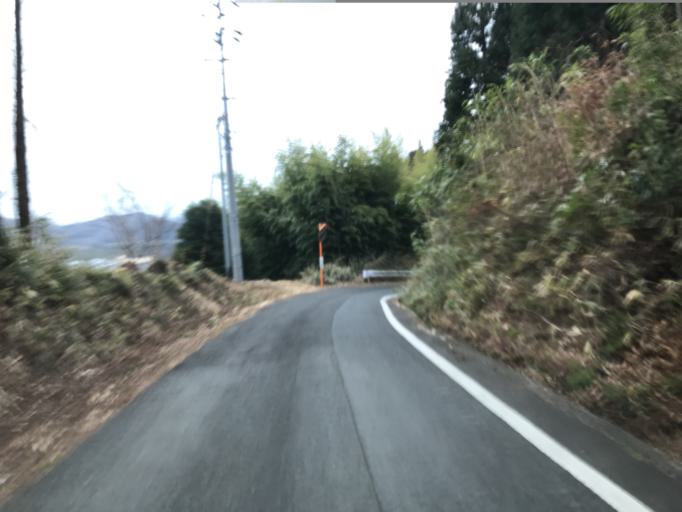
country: JP
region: Fukushima
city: Iwaki
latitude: 37.0545
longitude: 140.7888
